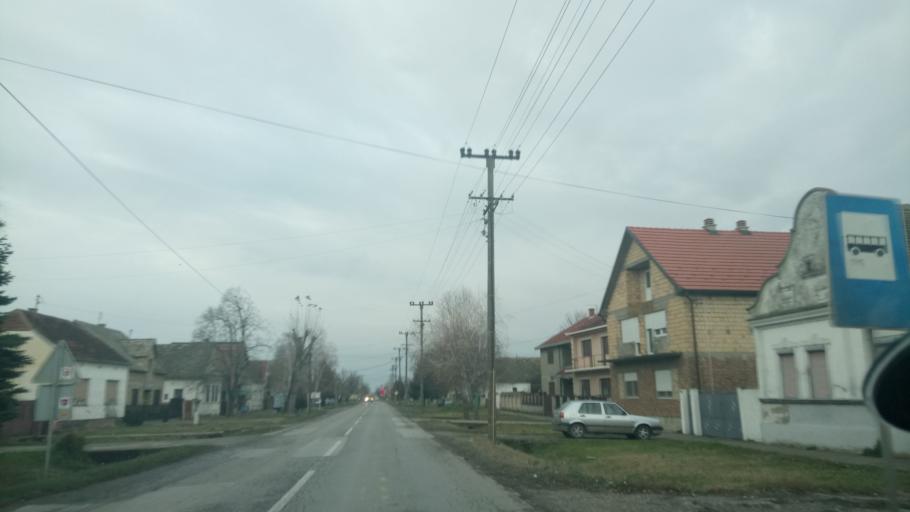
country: RS
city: Vojka
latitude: 44.9452
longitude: 20.1539
